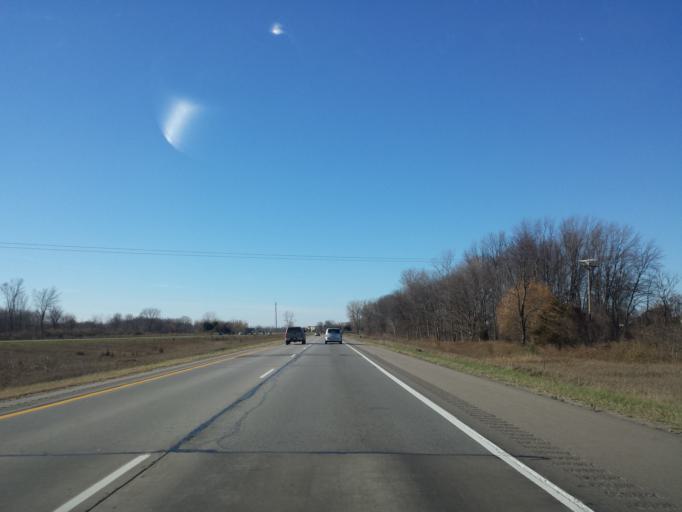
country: US
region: Michigan
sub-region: Livingston County
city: Fowlerville
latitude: 42.6434
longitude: -84.0433
